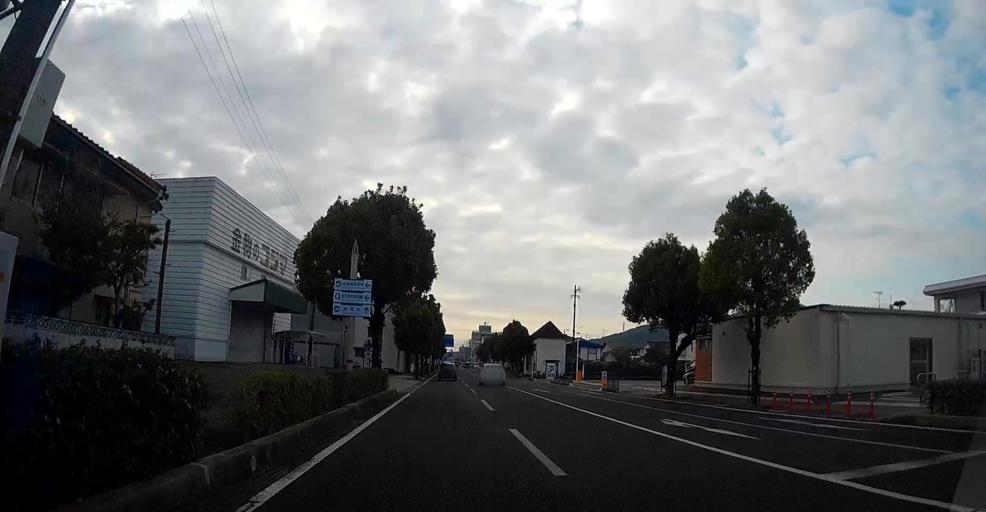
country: JP
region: Kumamoto
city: Hondo
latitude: 32.4614
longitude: 130.1914
